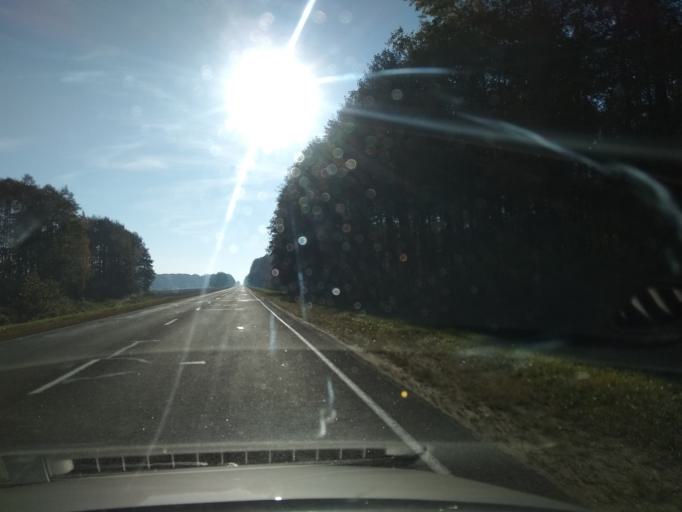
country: BY
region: Brest
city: Malaryta
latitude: 51.8816
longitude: 24.1606
